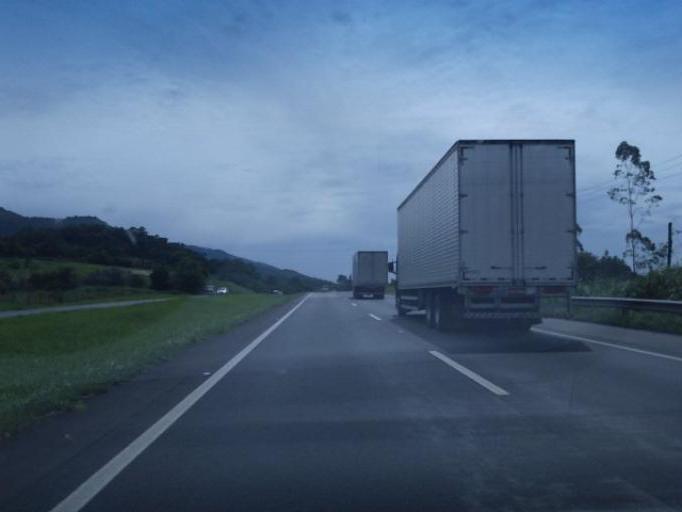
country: BR
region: Sao Paulo
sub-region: Miracatu
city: Miracatu
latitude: -24.2784
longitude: -47.4203
